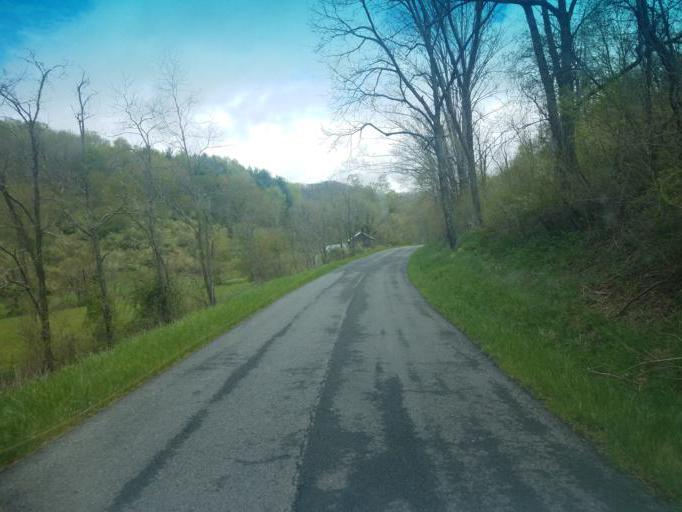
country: US
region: Virginia
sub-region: Smyth County
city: Atkins
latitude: 36.9804
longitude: -81.3953
